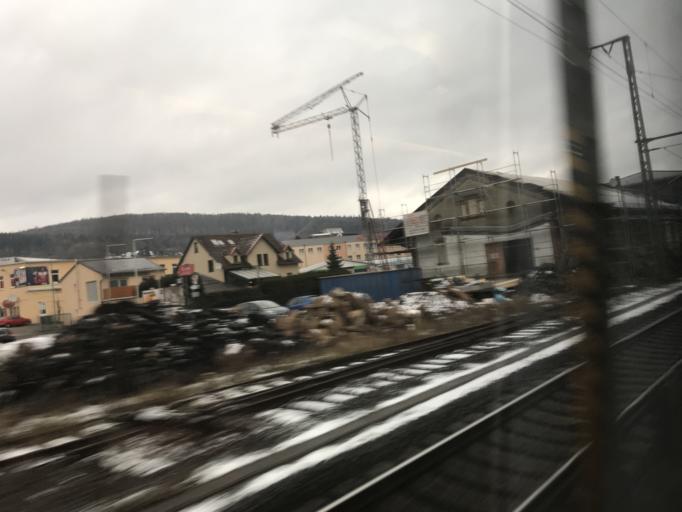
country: DE
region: Hesse
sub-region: Regierungsbezirk Darmstadt
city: Wachtersbach
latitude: 50.2546
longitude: 9.2962
